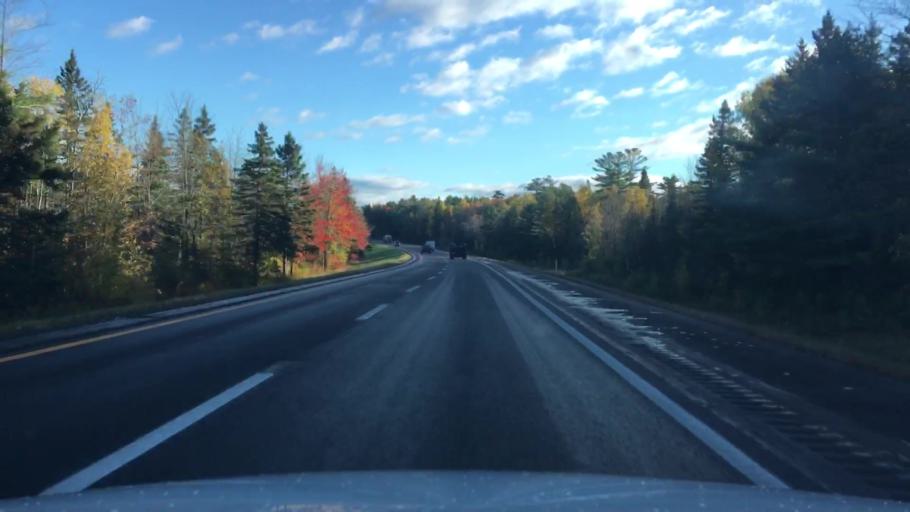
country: US
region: Maine
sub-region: Penobscot County
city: Veazie
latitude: 44.8625
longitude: -68.7129
